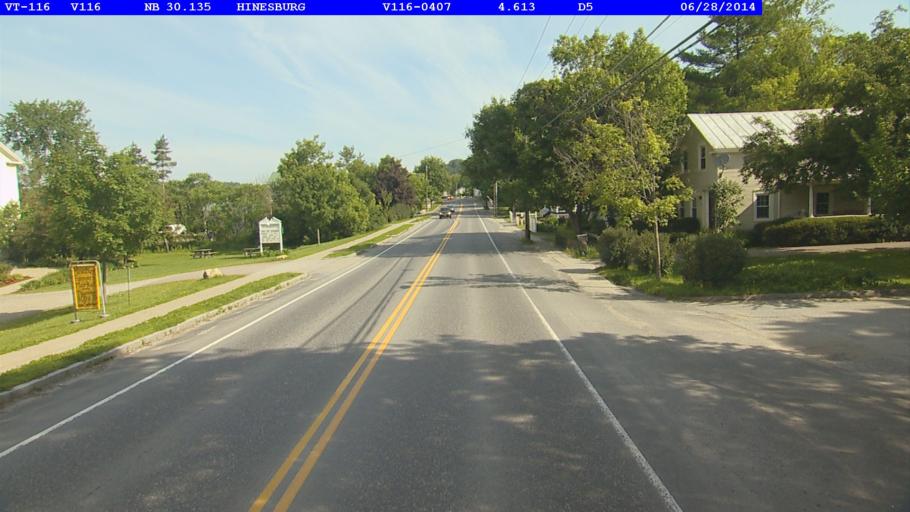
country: US
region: Vermont
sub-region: Chittenden County
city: Hinesburg
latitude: 44.3299
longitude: -73.1104
